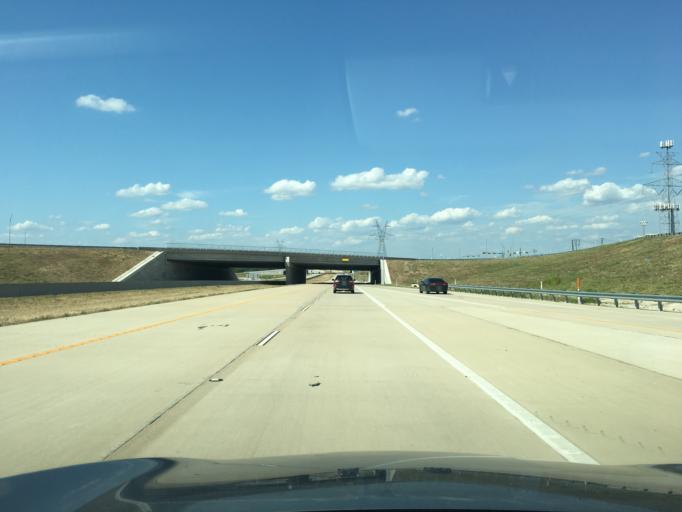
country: US
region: Texas
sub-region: Tarrant County
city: Mansfield
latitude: 32.5755
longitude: -97.0807
